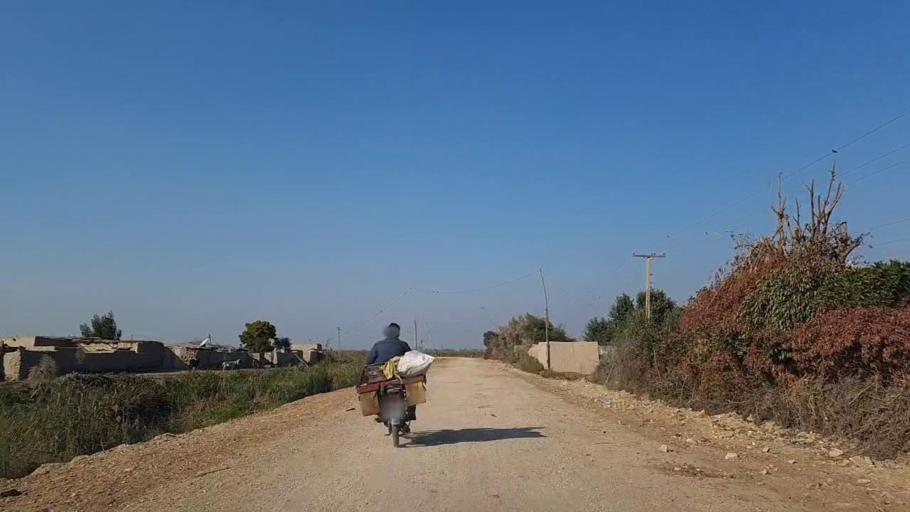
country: PK
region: Sindh
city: Bandhi
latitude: 26.6059
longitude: 68.3131
